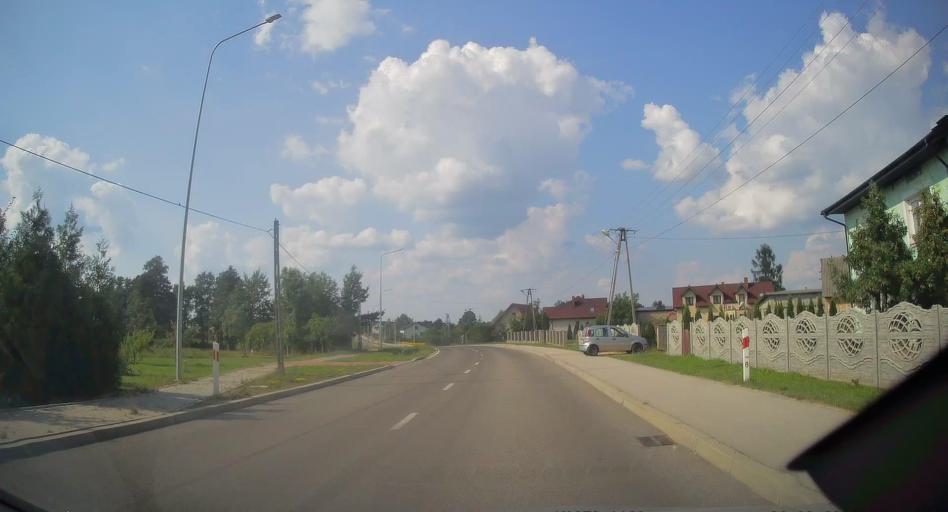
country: PL
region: Swietokrzyskie
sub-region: Powiat konecki
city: Radoszyce
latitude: 51.0297
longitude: 20.2898
